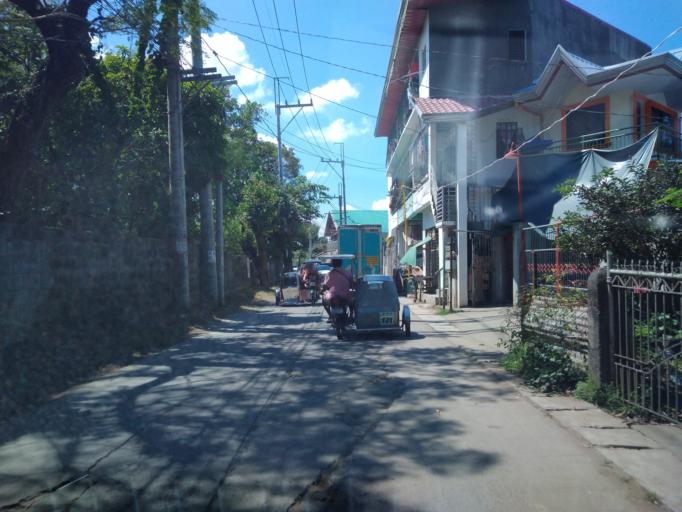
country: PH
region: Central Luzon
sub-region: Province of Bulacan
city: Balasing
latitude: 14.8555
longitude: 121.0137
